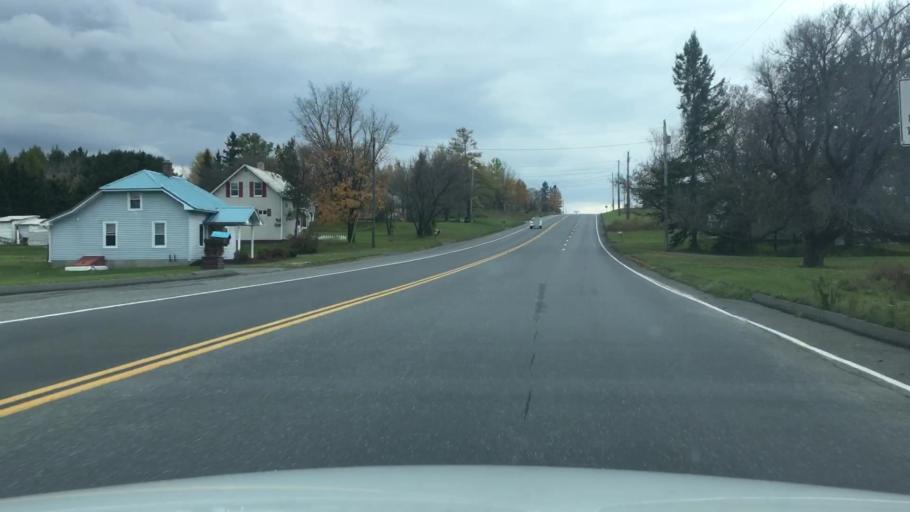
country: US
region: Maine
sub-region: Aroostook County
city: Caribou
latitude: 46.7832
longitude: -67.9890
